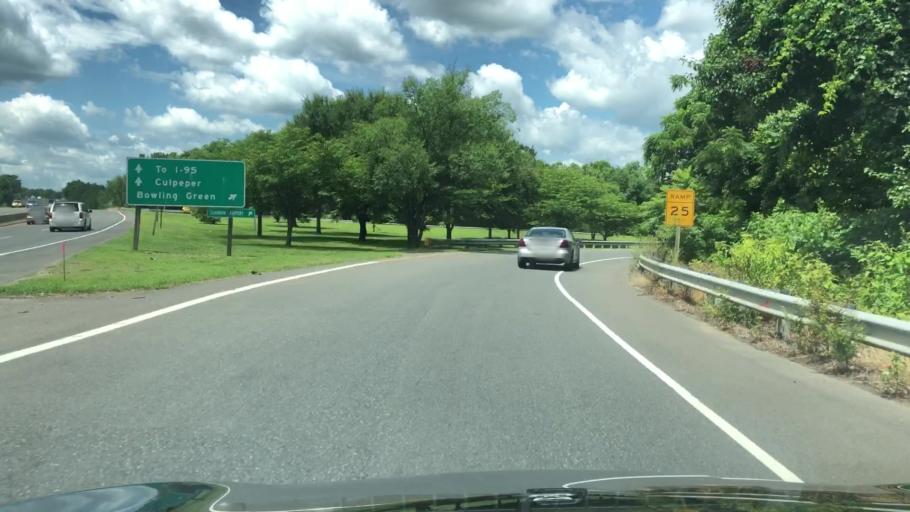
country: US
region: Virginia
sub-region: City of Fredericksburg
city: Fredericksburg
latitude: 38.2905
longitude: -77.4541
